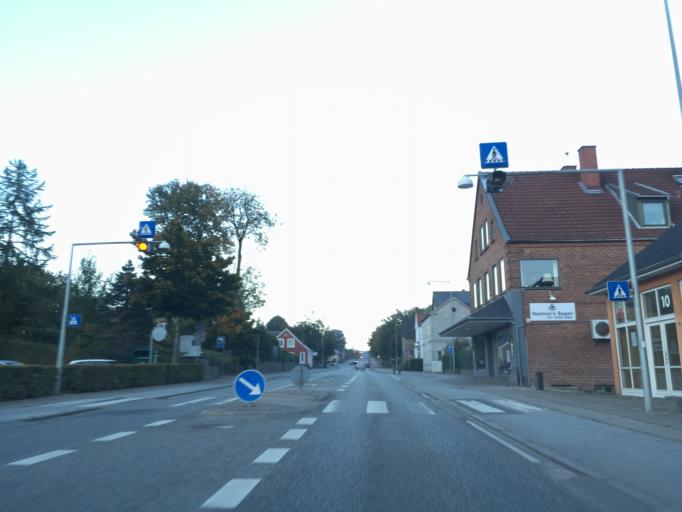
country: DK
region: South Denmark
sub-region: Aabenraa Kommune
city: Aabenraa
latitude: 55.0504
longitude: 9.4219
